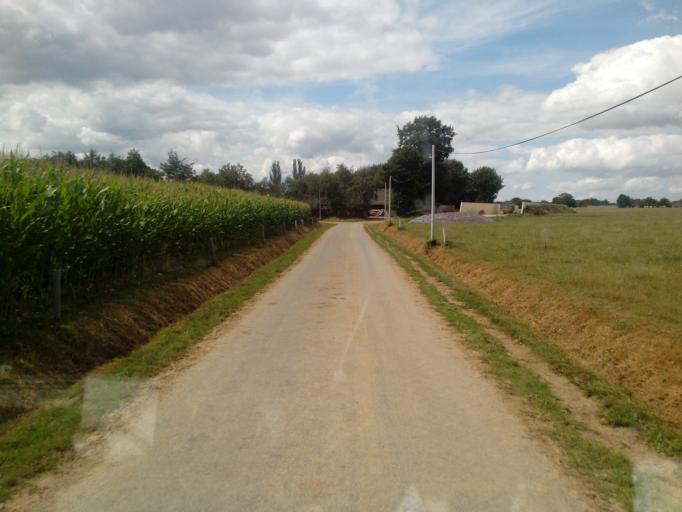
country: FR
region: Brittany
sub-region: Departement du Morbihan
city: Guilliers
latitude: 48.1027
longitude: -2.4014
